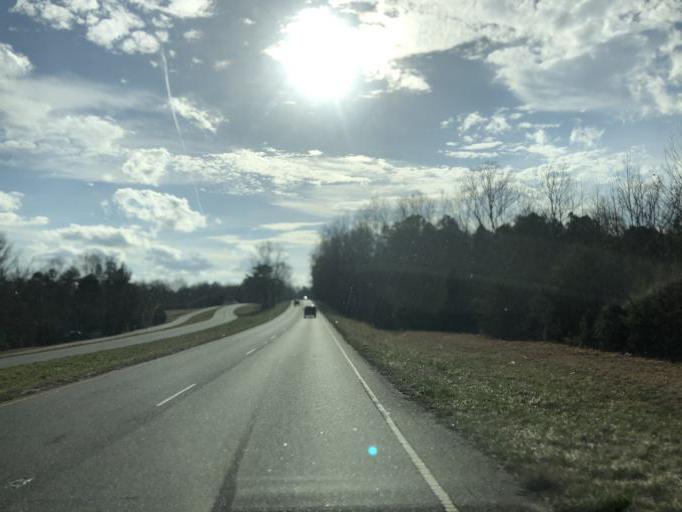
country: US
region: North Carolina
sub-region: Gaston County
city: Bessemer City
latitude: 35.2522
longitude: -81.2810
